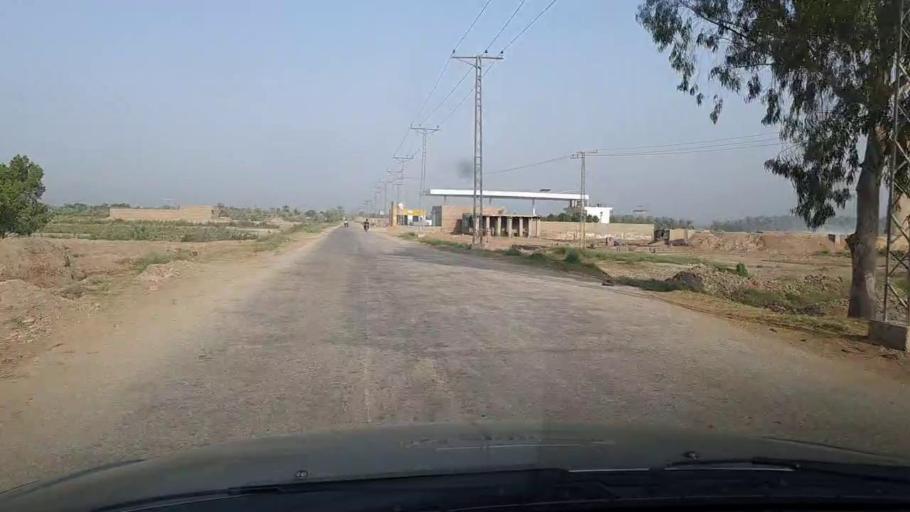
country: PK
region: Sindh
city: Pir jo Goth
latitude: 27.5690
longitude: 68.6354
